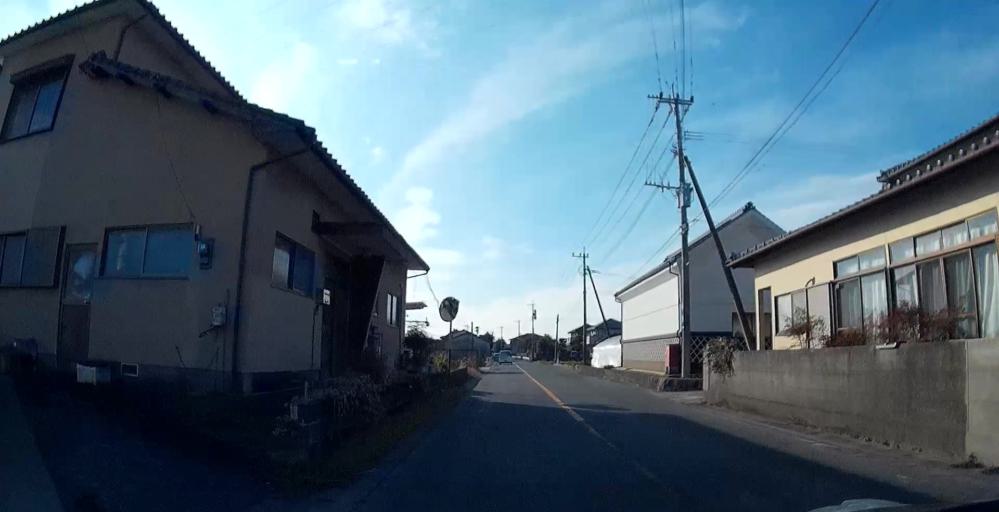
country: JP
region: Kumamoto
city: Uto
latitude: 32.7320
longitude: 130.6434
